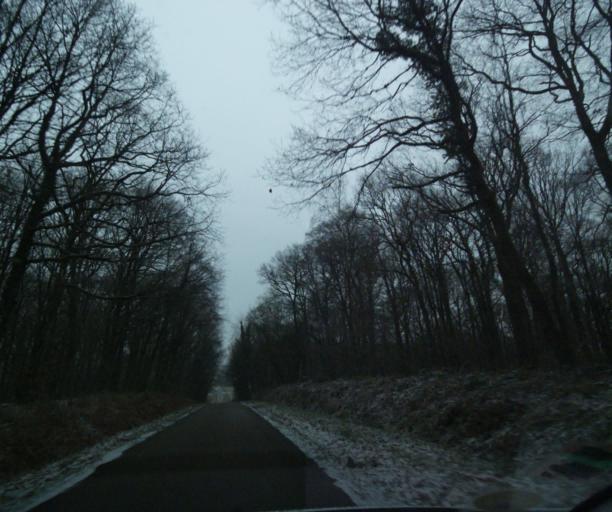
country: FR
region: Champagne-Ardenne
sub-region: Departement de la Haute-Marne
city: Wassy
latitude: 48.4755
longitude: 5.0253
